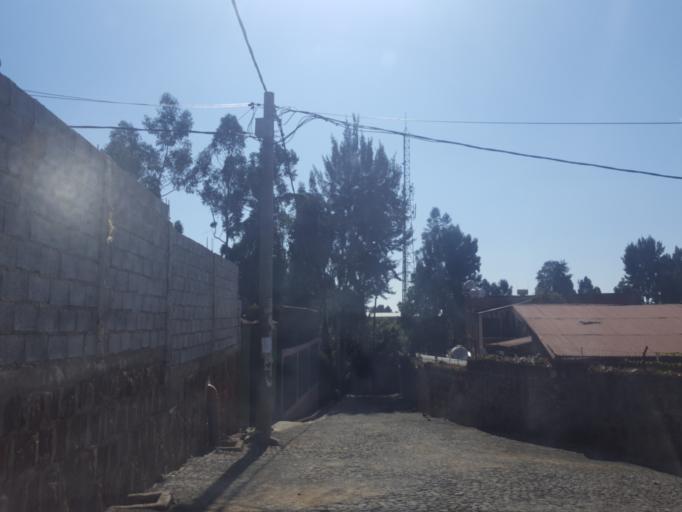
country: ET
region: Adis Abeba
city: Addis Ababa
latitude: 9.0562
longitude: 38.7378
